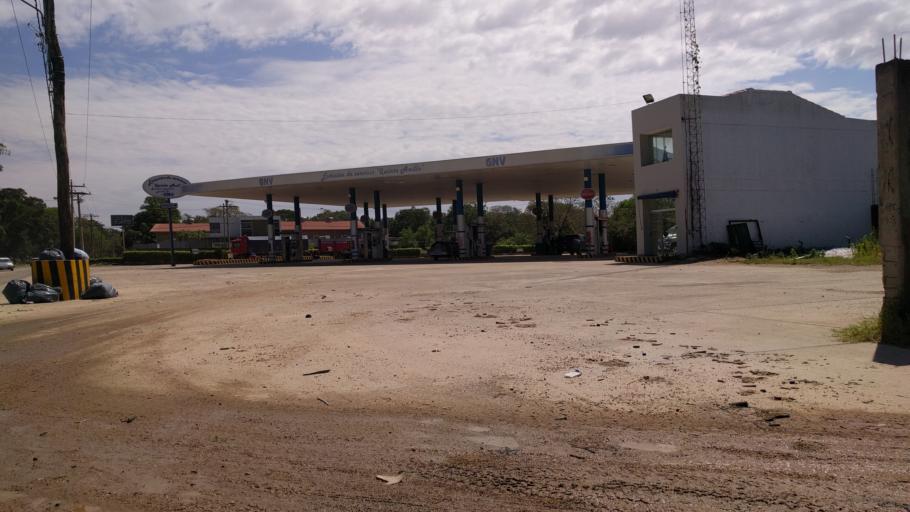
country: BO
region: Santa Cruz
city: Santa Cruz de la Sierra
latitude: -17.8051
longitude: -63.2253
